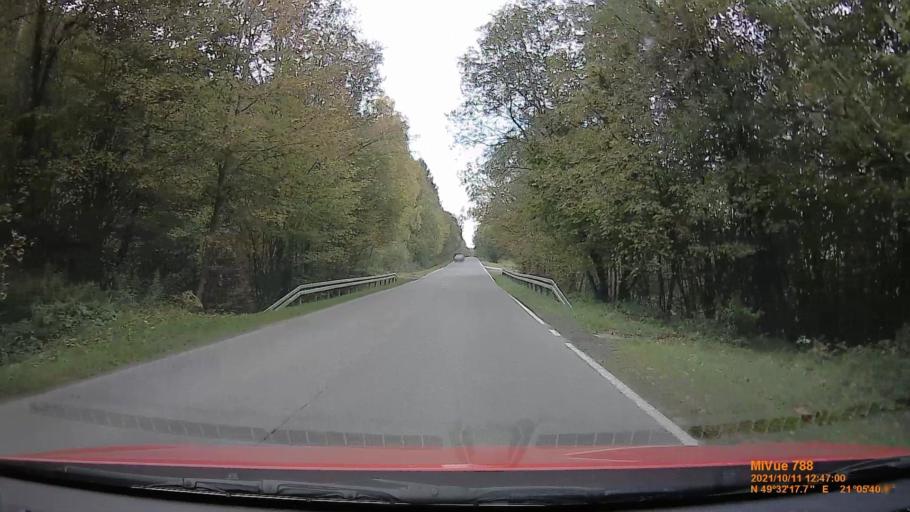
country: PL
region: Lesser Poland Voivodeship
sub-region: Powiat gorlicki
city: Uscie Gorlickie
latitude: 49.5384
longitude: 21.0945
